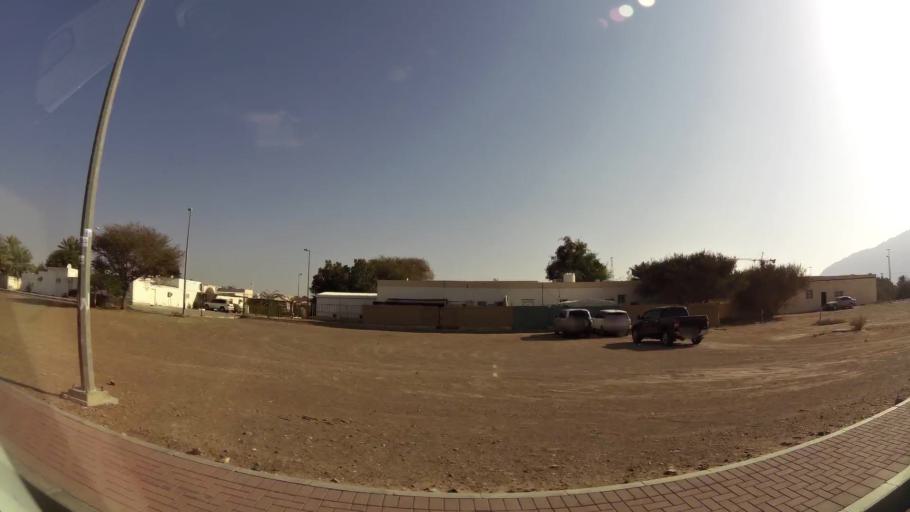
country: AE
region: Abu Dhabi
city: Al Ain
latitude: 24.0389
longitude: 55.8453
